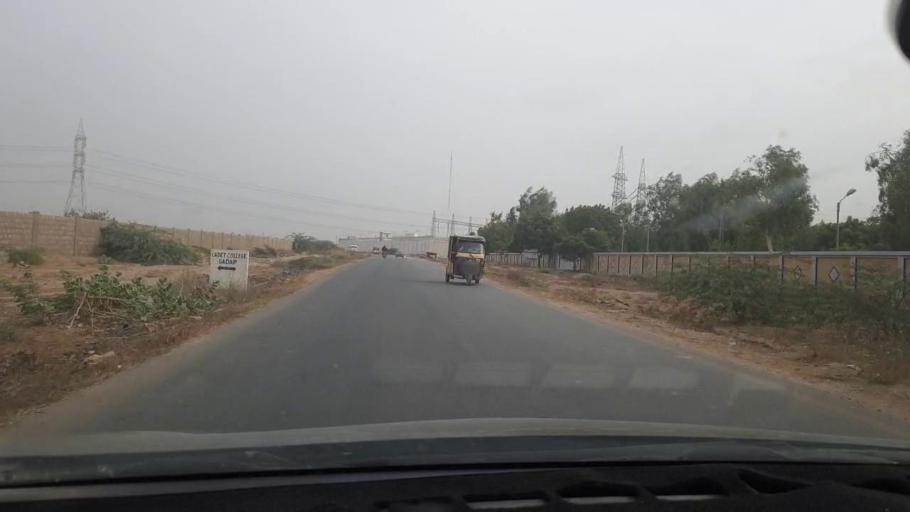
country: PK
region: Sindh
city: Malir Cantonment
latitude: 24.9120
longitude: 67.2801
